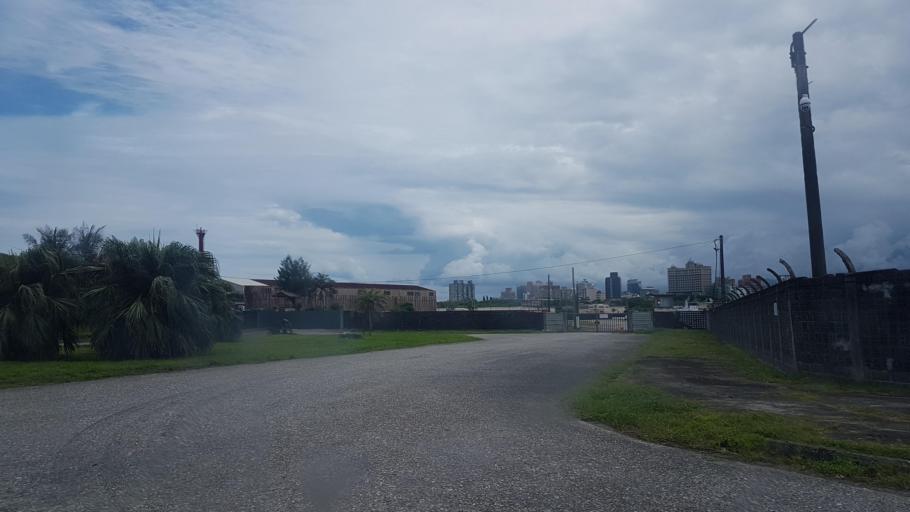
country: TW
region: Taiwan
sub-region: Hualien
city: Hualian
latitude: 24.0020
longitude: 121.6407
